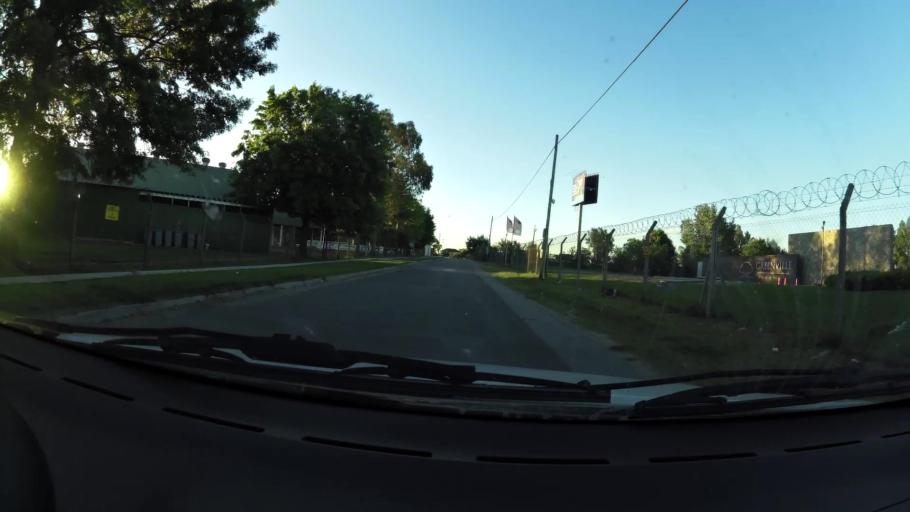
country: AR
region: Buenos Aires
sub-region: Partido de Quilmes
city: Quilmes
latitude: -34.8001
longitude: -58.1606
